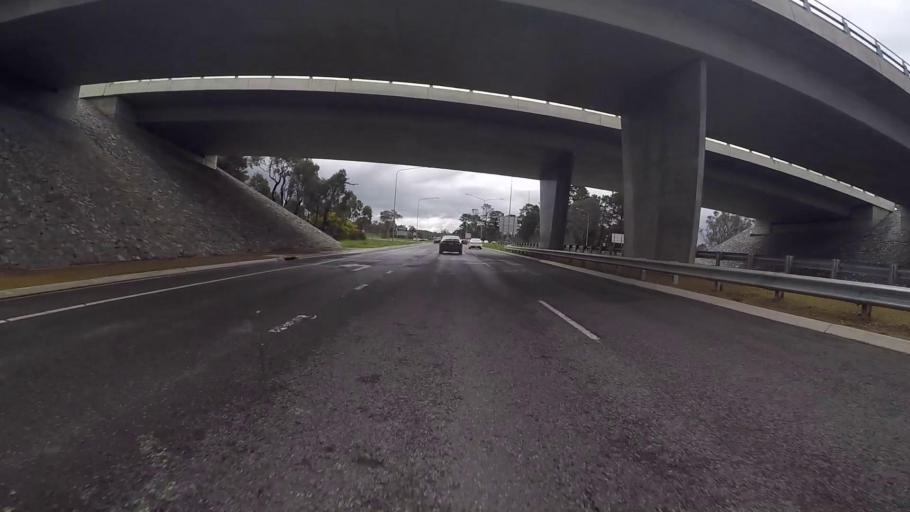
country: AU
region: Australian Capital Territory
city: Kaleen
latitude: -35.2257
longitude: 149.1223
